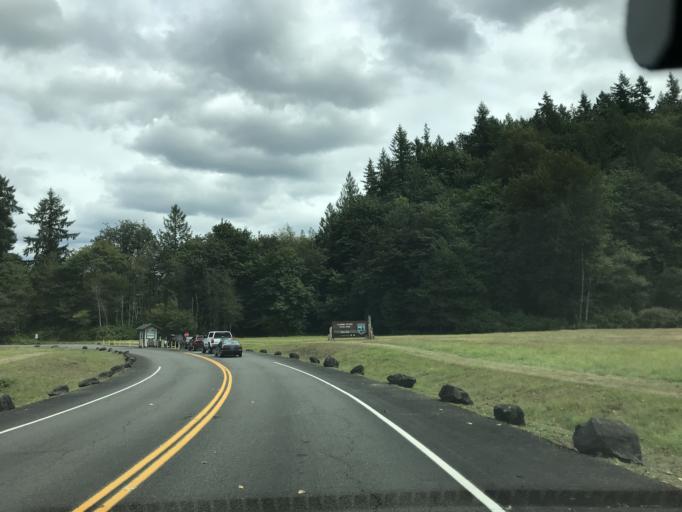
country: US
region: Washington
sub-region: King County
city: Black Diamond
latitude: 47.2785
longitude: -122.0376
